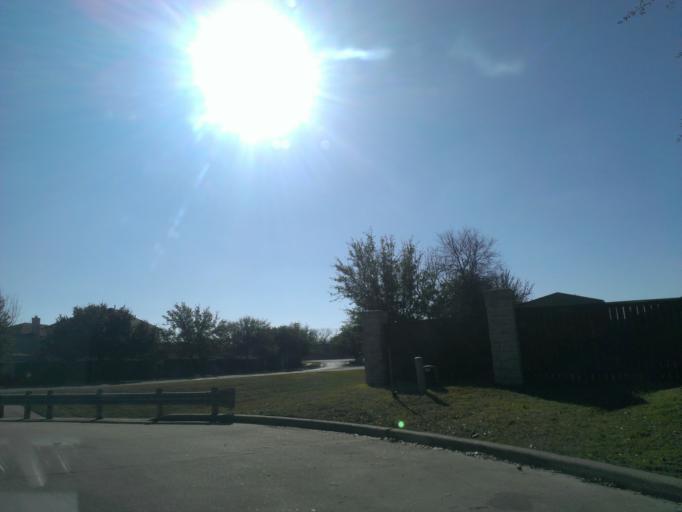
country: US
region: Texas
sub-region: Williamson County
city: Round Rock
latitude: 30.5318
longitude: -97.6200
